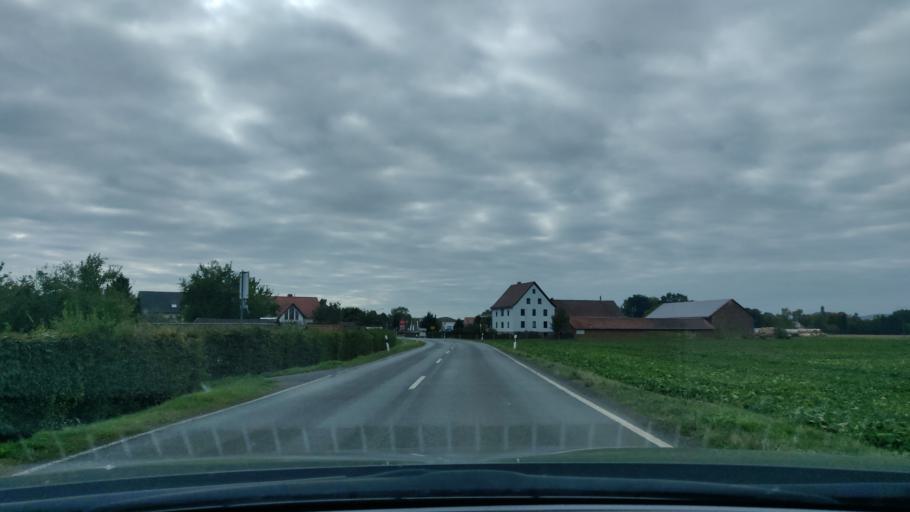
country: DE
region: Hesse
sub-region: Regierungsbezirk Kassel
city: Wabern
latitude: 51.1073
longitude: 9.3528
